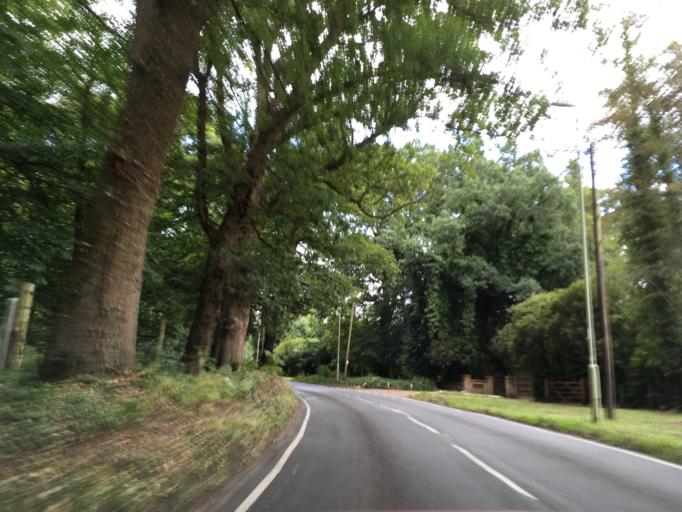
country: GB
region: England
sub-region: Hampshire
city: Chandlers Ford
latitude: 50.9989
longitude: -1.3602
